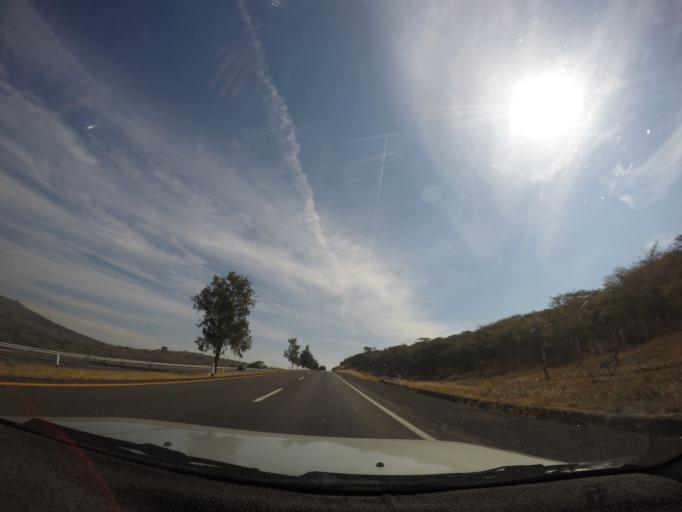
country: MX
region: Michoacan
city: Ecuandureo
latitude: 20.1815
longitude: -102.2779
